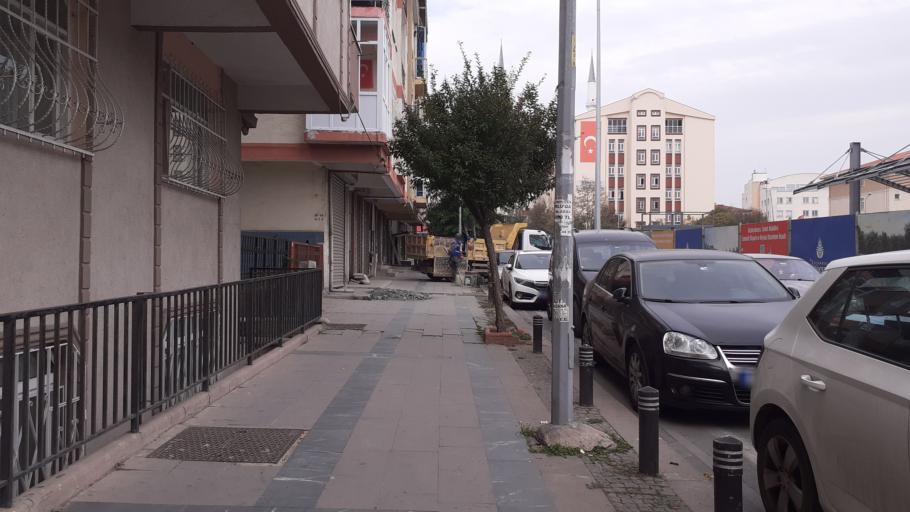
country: TR
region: Istanbul
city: Mahmutbey
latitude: 40.9899
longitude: 28.7828
